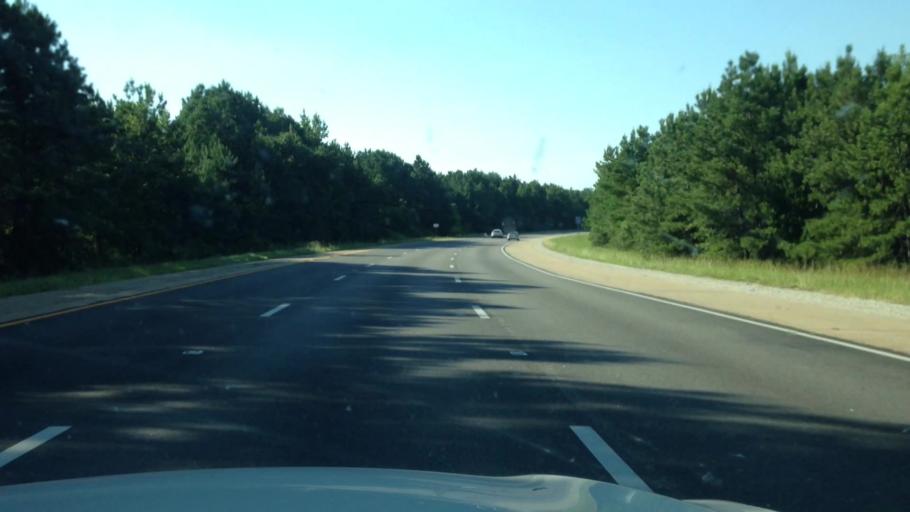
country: US
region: Virginia
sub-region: Prince George County
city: Fort Lee
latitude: 37.2728
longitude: -77.3296
